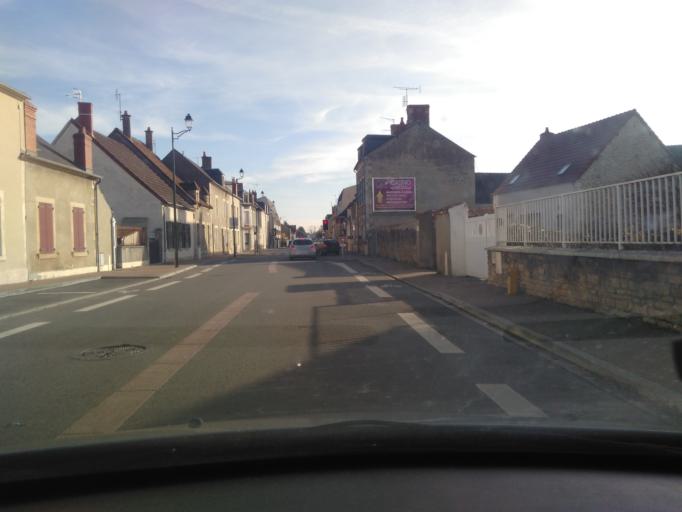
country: FR
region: Centre
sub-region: Departement du Cher
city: Saint-Amand-Montrond
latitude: 46.7242
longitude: 2.5087
